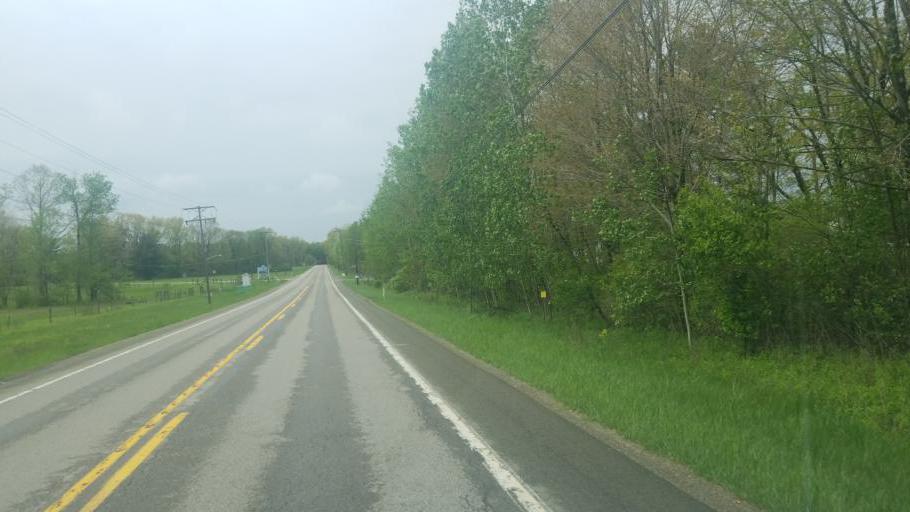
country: US
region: Pennsylvania
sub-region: Forest County
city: Marienville
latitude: 41.3965
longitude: -79.2587
